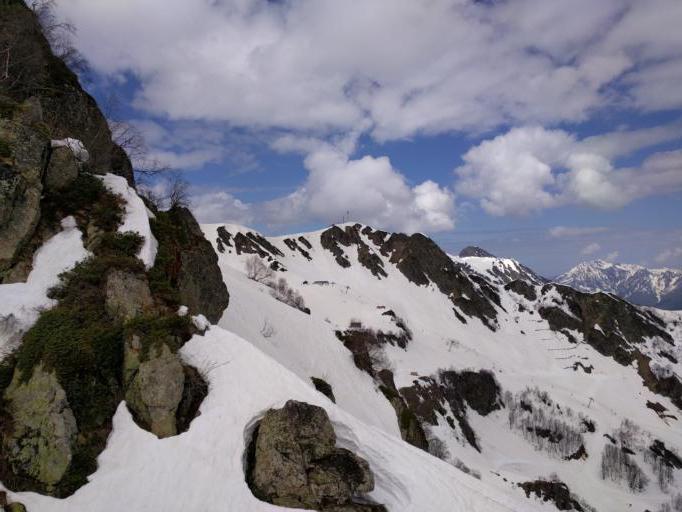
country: RU
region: Krasnodarskiy
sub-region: Sochi City
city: Krasnaya Polyana
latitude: 43.6281
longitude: 40.3106
